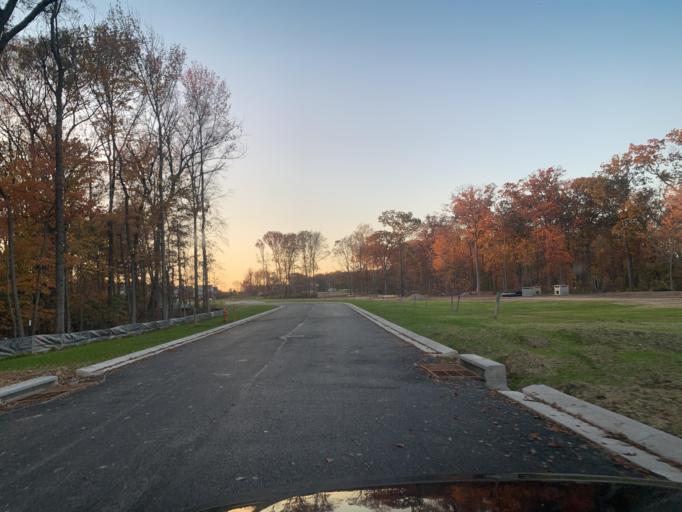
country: US
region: Maryland
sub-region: Baltimore County
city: Middle River
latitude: 39.3161
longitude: -76.4372
